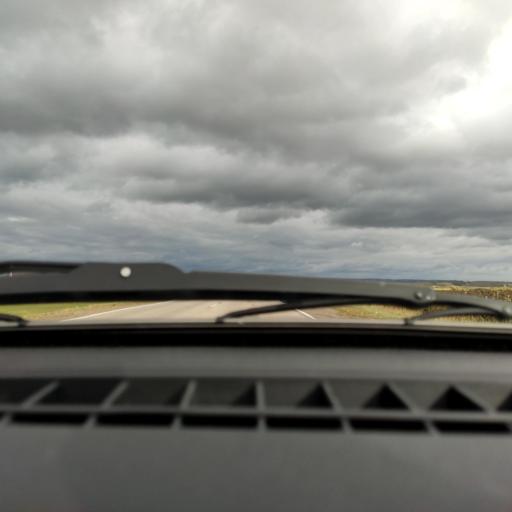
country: RU
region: Bashkortostan
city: Shafranovo
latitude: 54.0137
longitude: 54.8571
